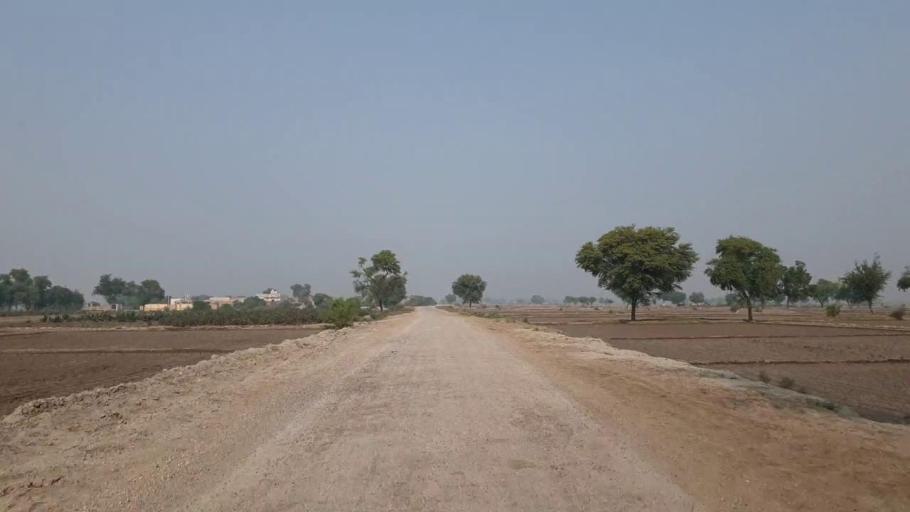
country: PK
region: Sindh
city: Bhan
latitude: 26.5115
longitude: 67.6895
